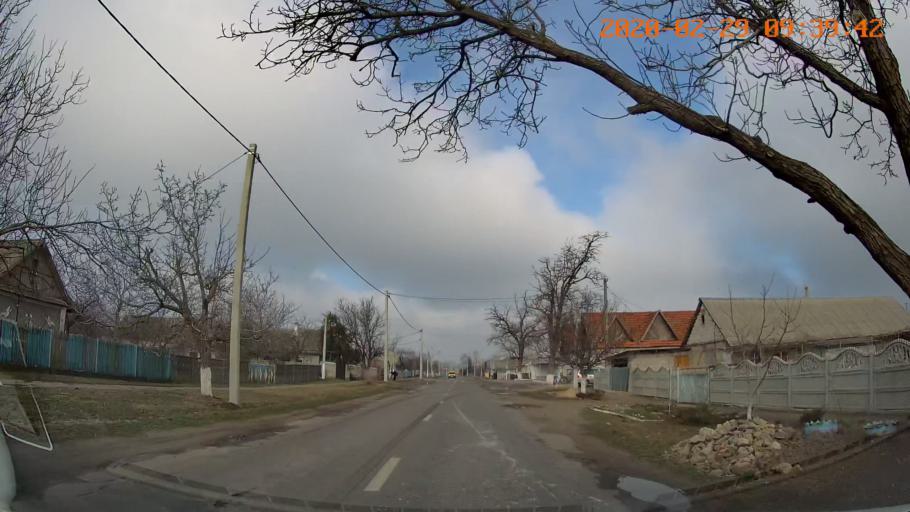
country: MD
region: Telenesti
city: Crasnoe
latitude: 46.6368
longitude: 29.8517
